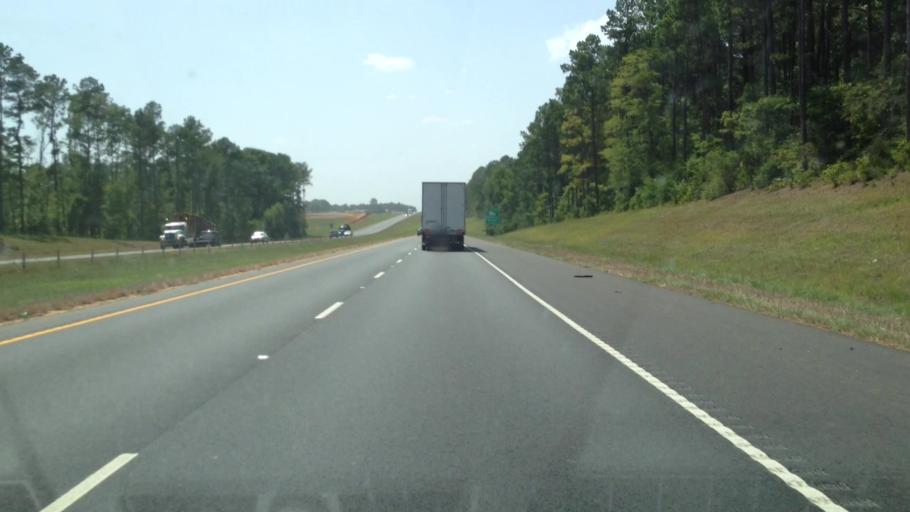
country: US
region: Louisiana
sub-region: Webster Parish
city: Minden
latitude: 32.5774
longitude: -93.2327
